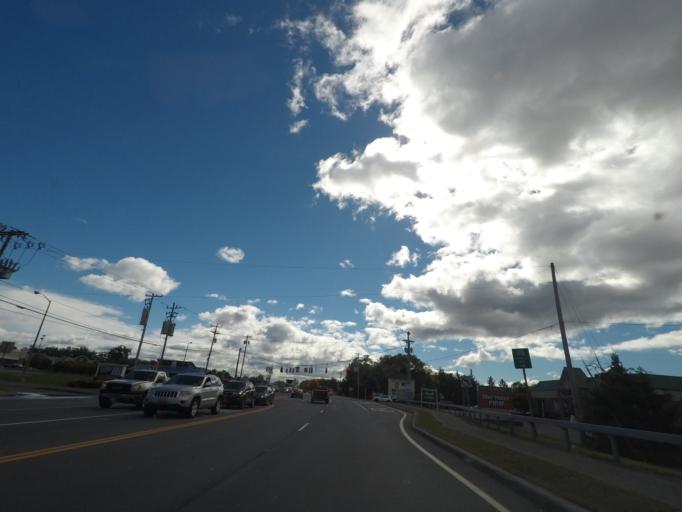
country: US
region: New York
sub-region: Saratoga County
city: Country Knolls
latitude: 42.8626
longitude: -73.7688
